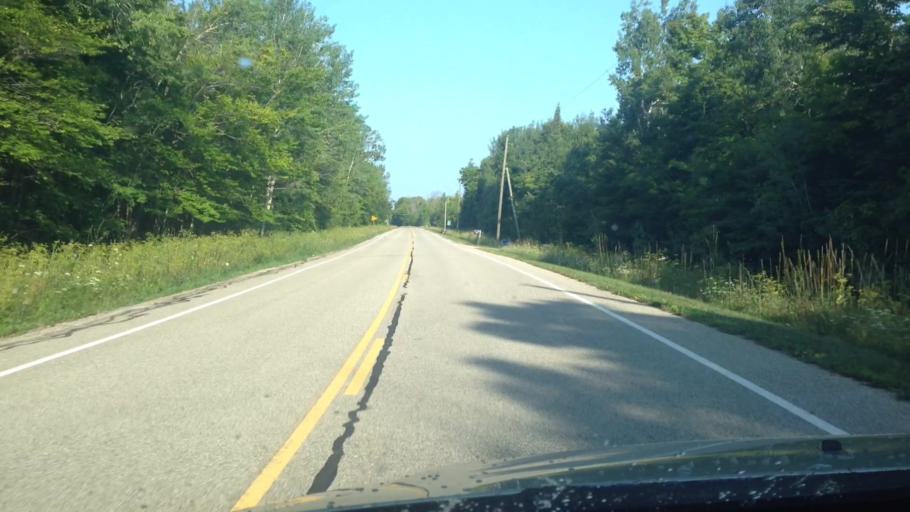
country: US
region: Michigan
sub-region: Mackinac County
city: Saint Ignace
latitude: 45.8926
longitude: -84.7971
